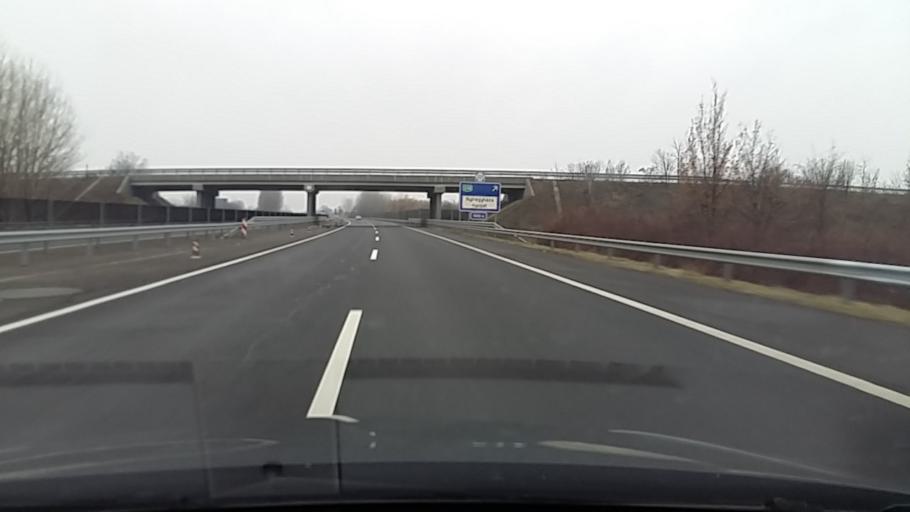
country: HU
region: Szabolcs-Szatmar-Bereg
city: Nyiregyhaza
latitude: 47.9010
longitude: 21.6686
